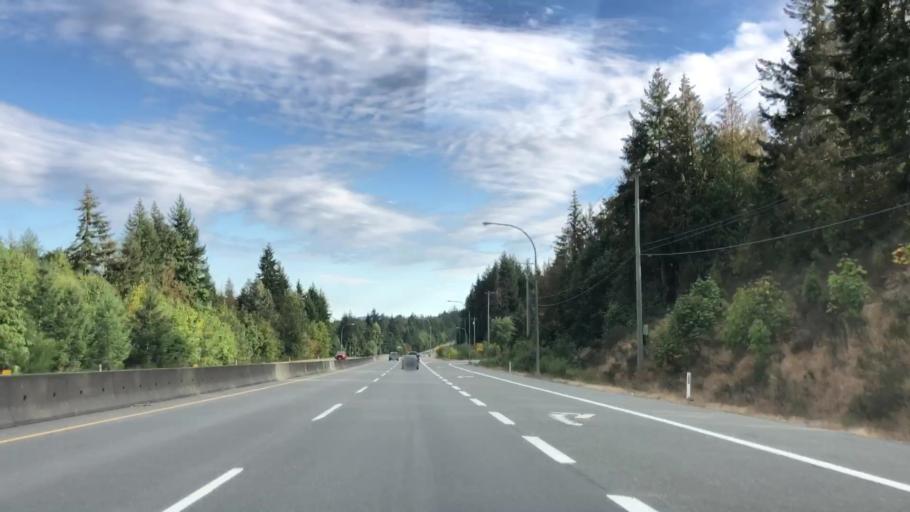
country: CA
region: British Columbia
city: North Saanich
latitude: 48.6160
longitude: -123.5422
